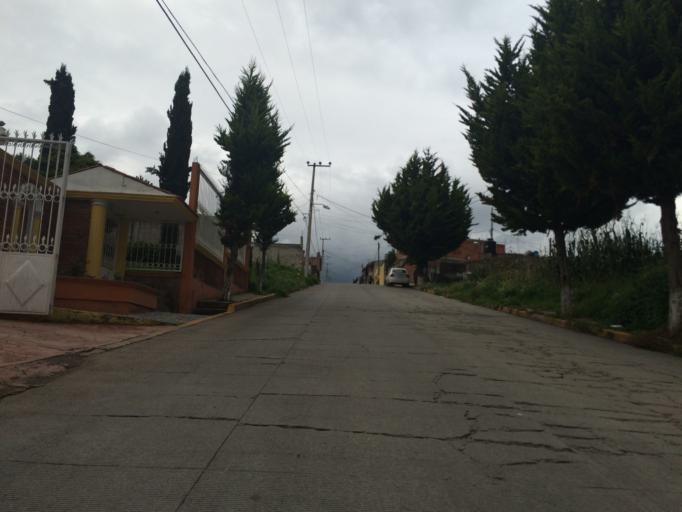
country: MX
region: Mexico
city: San Juan de las Huertas
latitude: 19.2486
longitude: -99.7460
